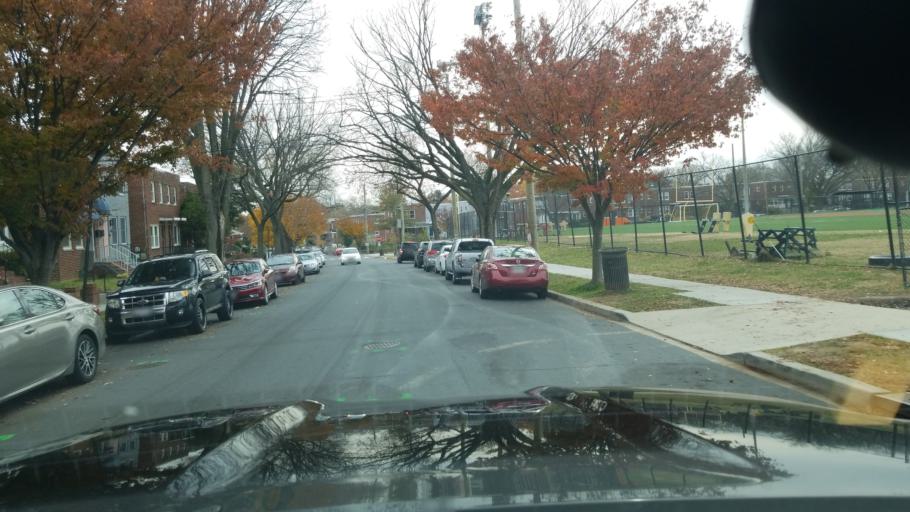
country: US
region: Maryland
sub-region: Prince George's County
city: Chillum
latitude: 38.9601
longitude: -76.9985
